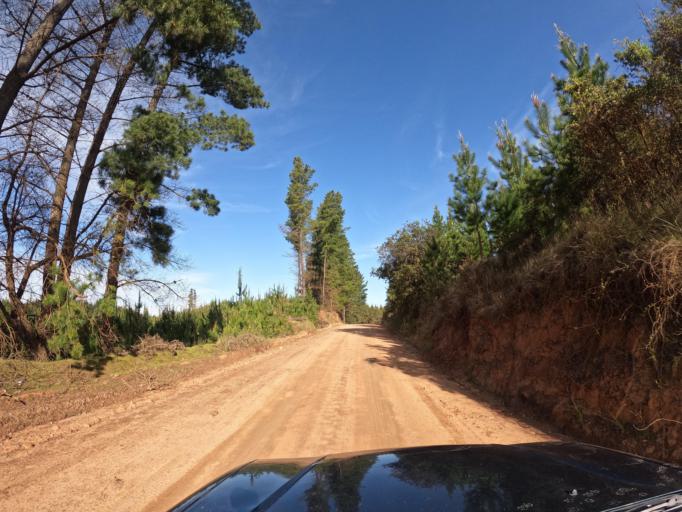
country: CL
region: Biobio
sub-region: Provincia de Biobio
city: La Laja
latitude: -37.1120
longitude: -72.7398
